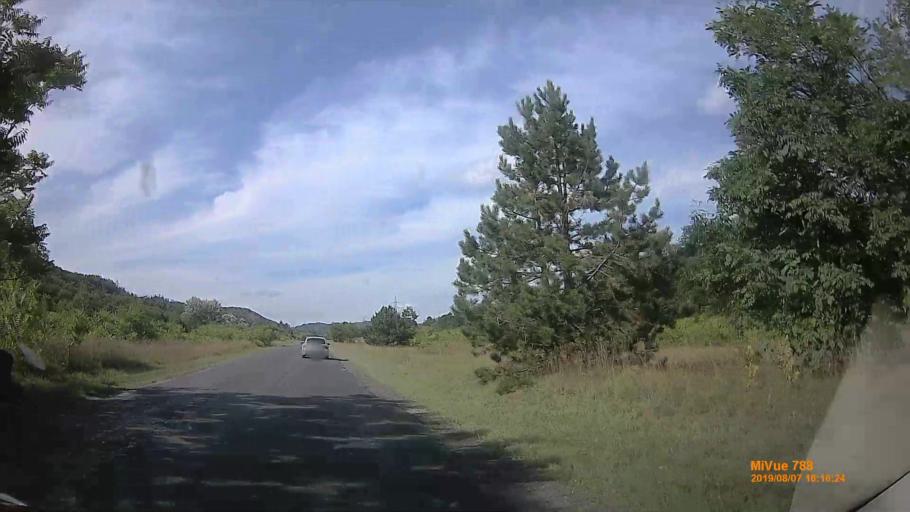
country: HU
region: Zala
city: Gyenesdias
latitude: 46.8125
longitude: 17.2702
